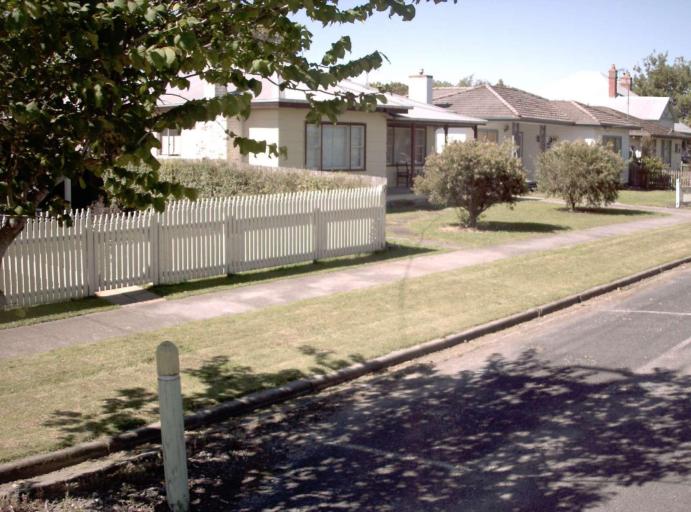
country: AU
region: Victoria
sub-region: Latrobe
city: Morwell
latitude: -38.6652
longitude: 146.4388
